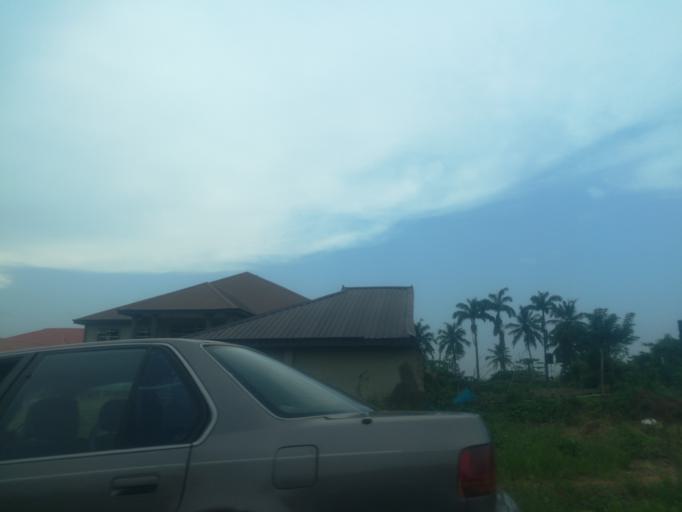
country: NG
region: Oyo
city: Ibadan
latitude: 7.3662
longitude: 3.8267
